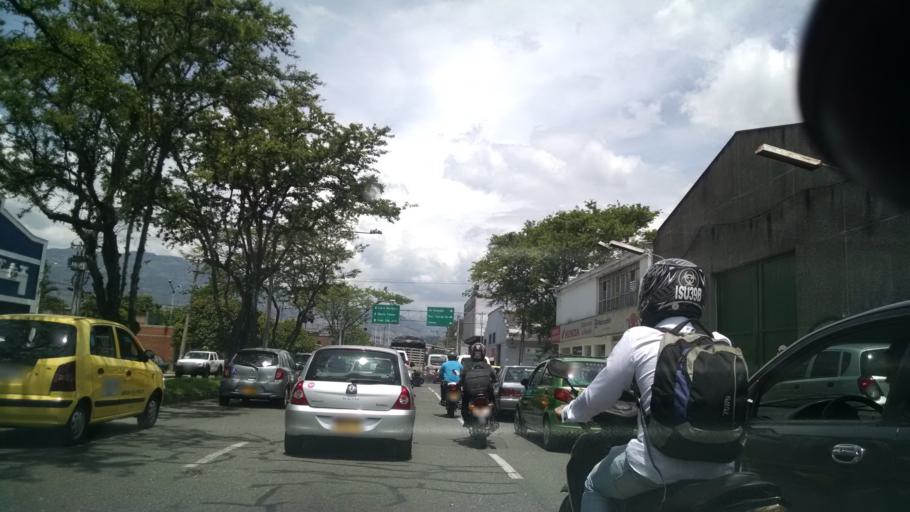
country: CO
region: Antioquia
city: Medellin
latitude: 6.2305
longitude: -75.5827
